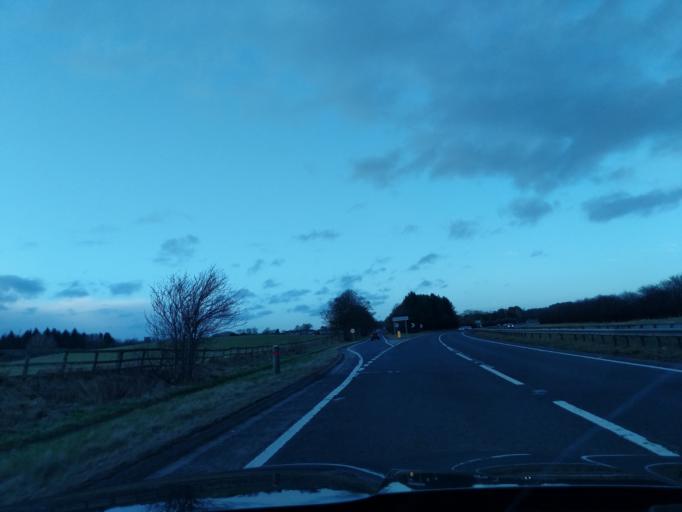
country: GB
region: England
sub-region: Northumberland
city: Stannington
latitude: 55.1025
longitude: -1.6634
